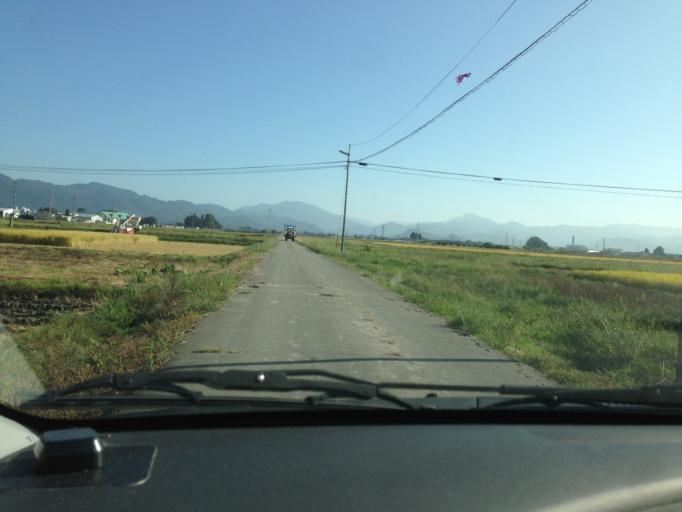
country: JP
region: Fukushima
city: Kitakata
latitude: 37.5160
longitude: 139.8994
